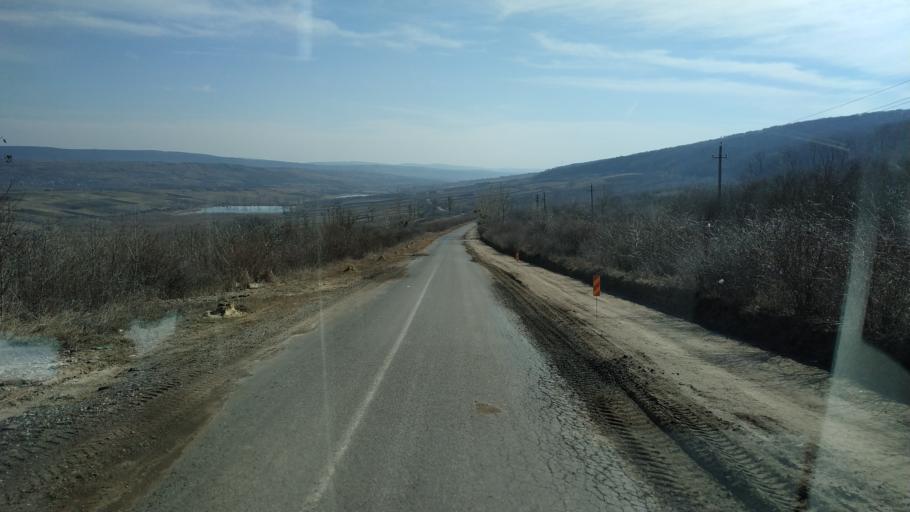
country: MD
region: Nisporeni
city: Nisporeni
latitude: 47.1901
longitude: 28.0685
